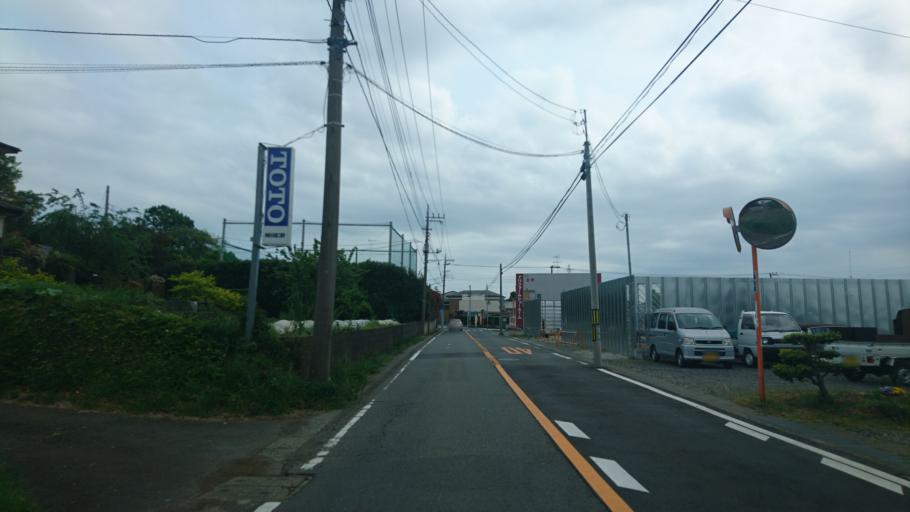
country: JP
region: Kanagawa
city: Fujisawa
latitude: 35.4113
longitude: 139.4783
